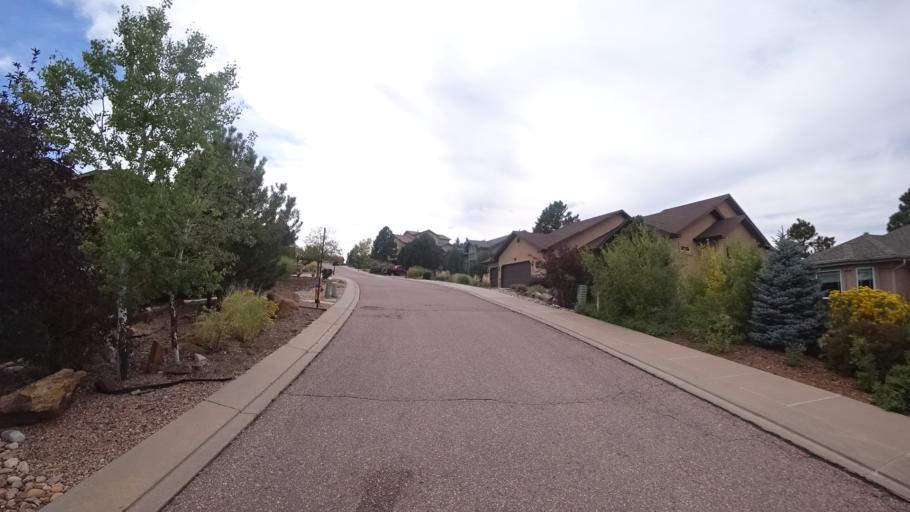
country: US
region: Colorado
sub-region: El Paso County
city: Colorado Springs
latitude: 38.9009
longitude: -104.7883
